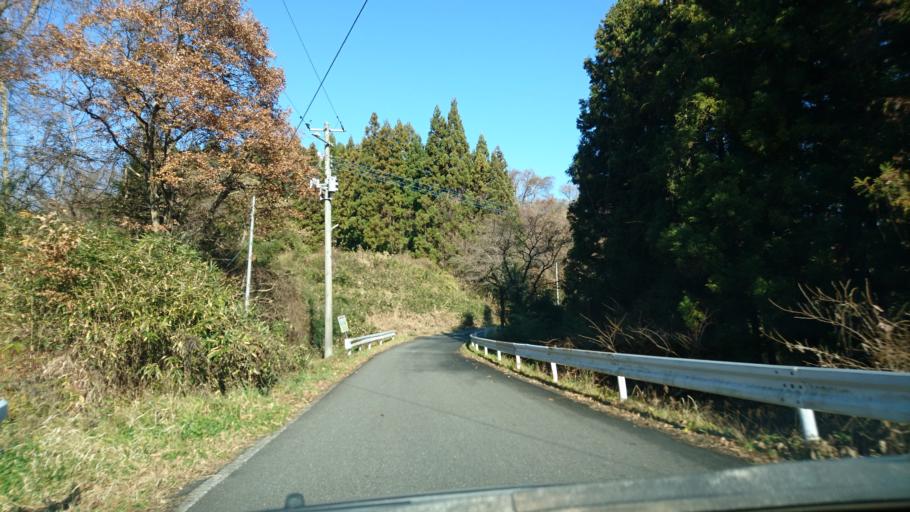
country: JP
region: Iwate
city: Ichinoseki
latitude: 38.9984
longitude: 141.0688
